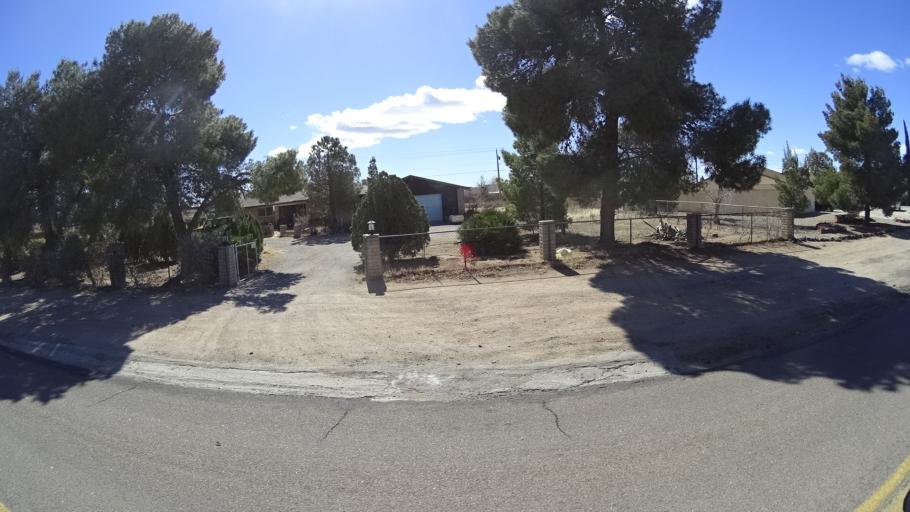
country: US
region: Arizona
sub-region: Mohave County
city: Kingman
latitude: 35.1990
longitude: -114.0095
